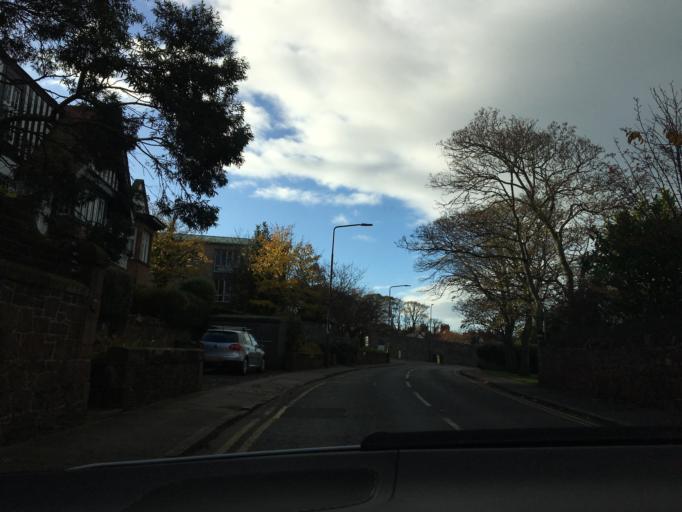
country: GB
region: Scotland
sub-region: East Lothian
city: North Berwick
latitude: 56.0566
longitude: -2.7263
